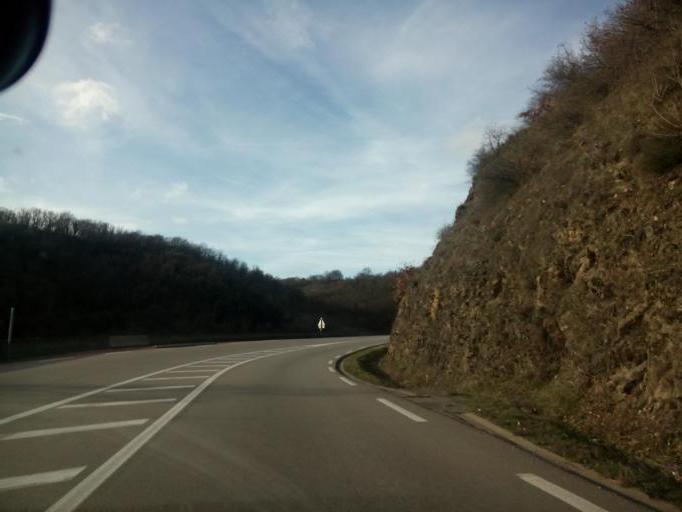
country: FR
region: Rhone-Alpes
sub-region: Departement de l'Ardeche
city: Serrieres
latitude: 45.3107
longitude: 4.7662
